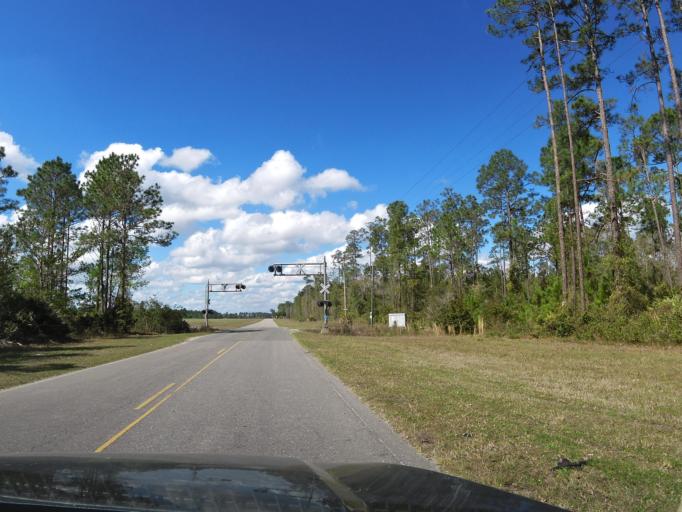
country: US
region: Florida
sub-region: Clay County
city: Green Cove Springs
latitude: 29.8680
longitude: -81.6759
